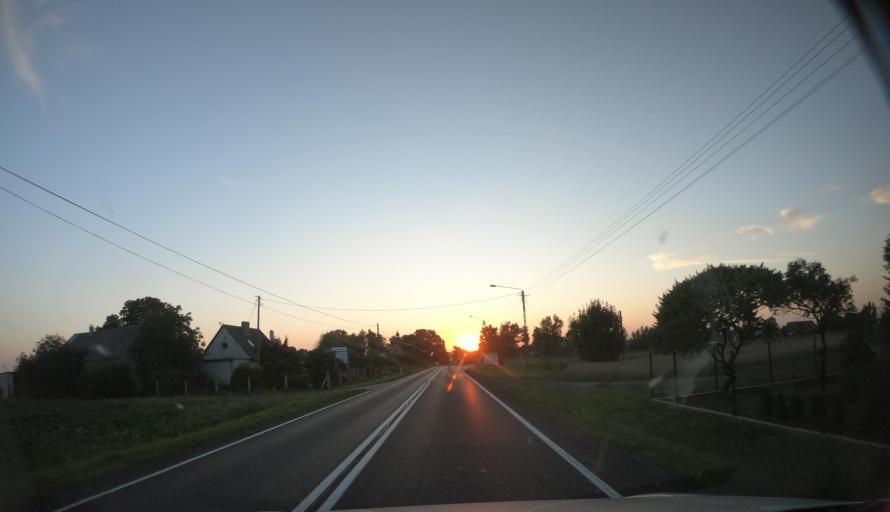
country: PL
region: Kujawsko-Pomorskie
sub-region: Powiat bydgoski
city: Koronowo
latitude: 53.3437
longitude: 17.8658
